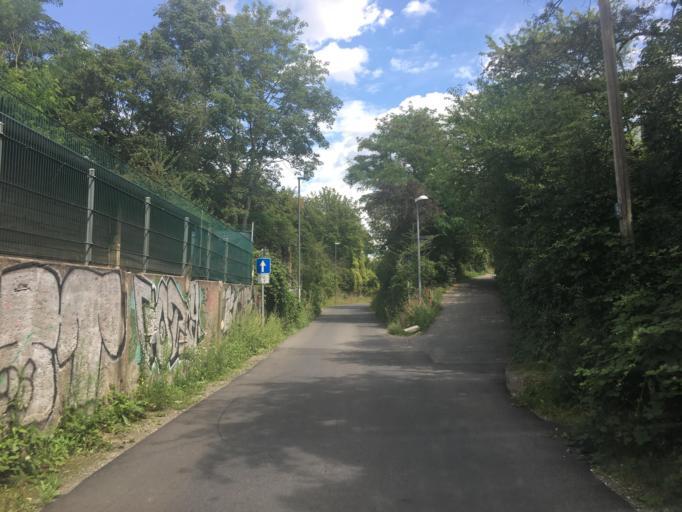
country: DE
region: North Rhine-Westphalia
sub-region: Regierungsbezirk Koln
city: Neustadt/Sued
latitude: 50.9014
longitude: 6.9284
